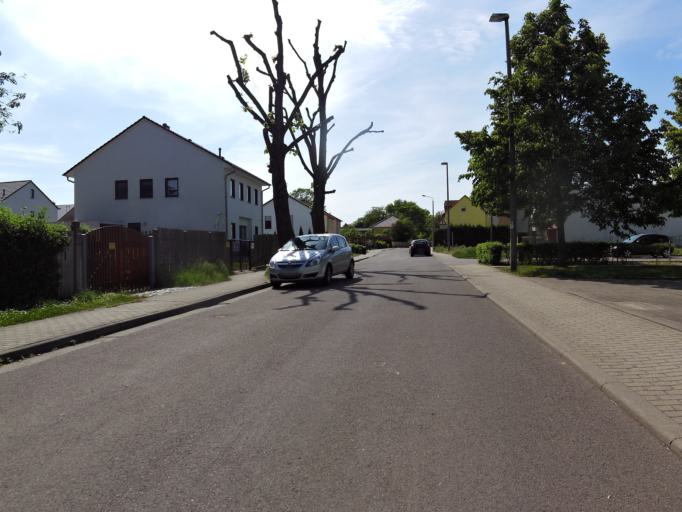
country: DE
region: Saxony
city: Leipzig
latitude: 51.3066
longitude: 12.4325
